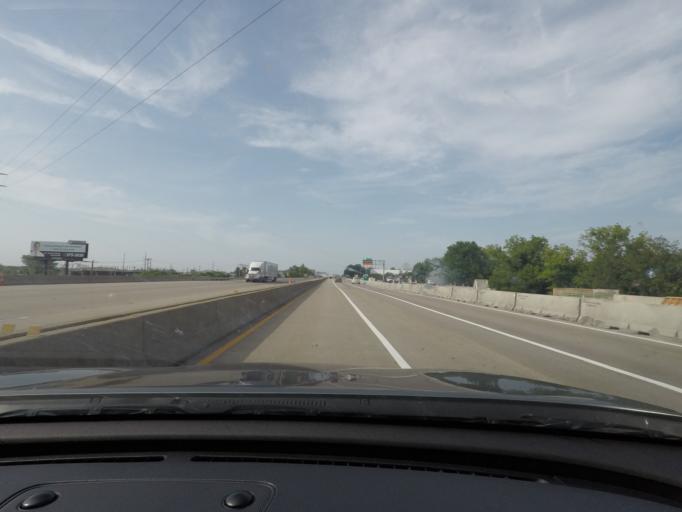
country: US
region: Missouri
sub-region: Saint Louis County
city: Maryland Heights
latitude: 38.7262
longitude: -90.4448
